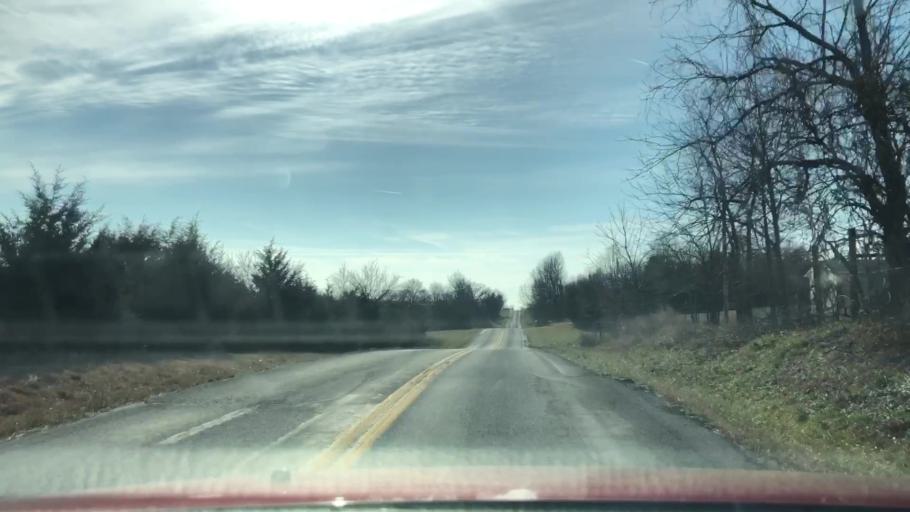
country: US
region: Missouri
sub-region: Wright County
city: Mansfield
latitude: 37.1101
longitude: -92.6294
